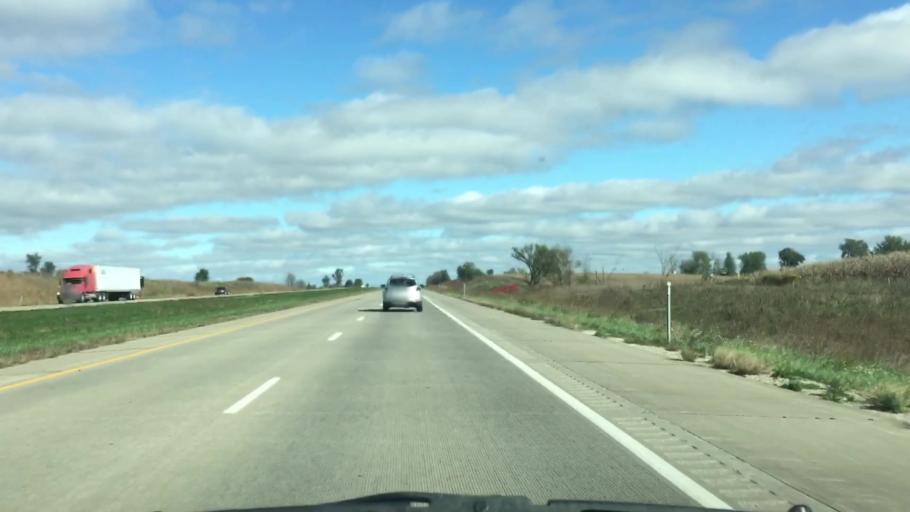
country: US
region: Iowa
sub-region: Decatur County
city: Leon
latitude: 40.7737
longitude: -93.8357
